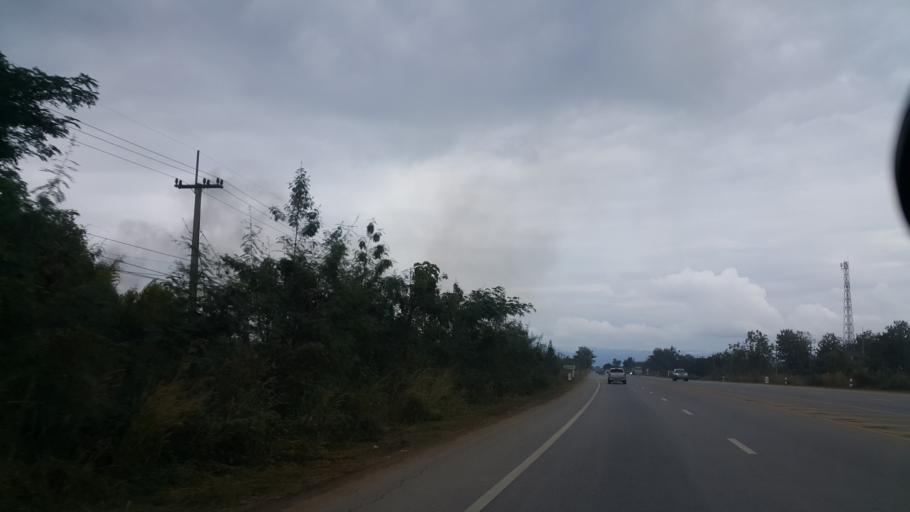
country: TH
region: Chiang Mai
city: San Kamphaeng
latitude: 18.7119
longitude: 99.1354
